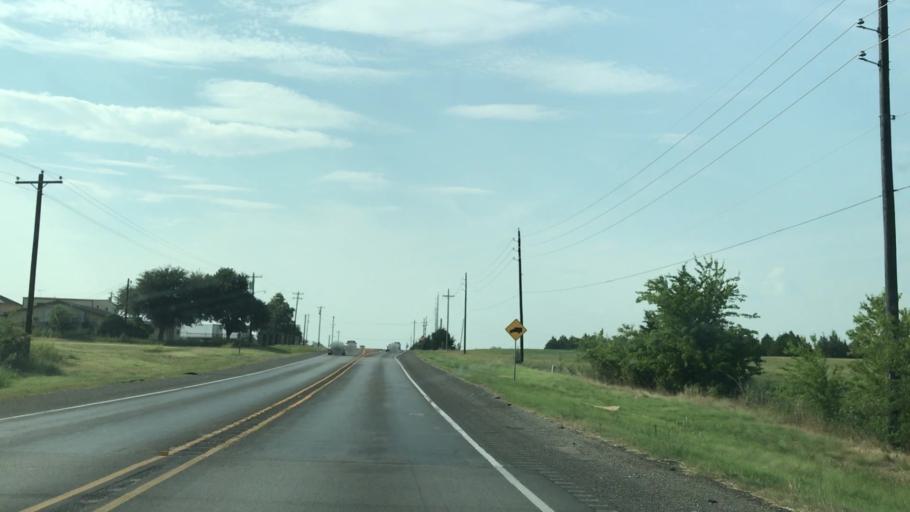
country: US
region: Texas
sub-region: Rockwall County
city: Rockwall
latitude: 32.8967
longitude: -96.4415
